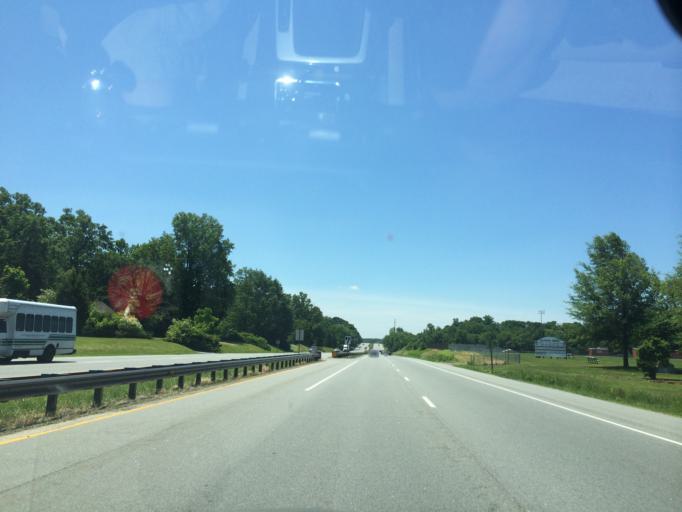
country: US
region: Maryland
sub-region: Talbot County
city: Easton
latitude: 38.7565
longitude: -76.0632
